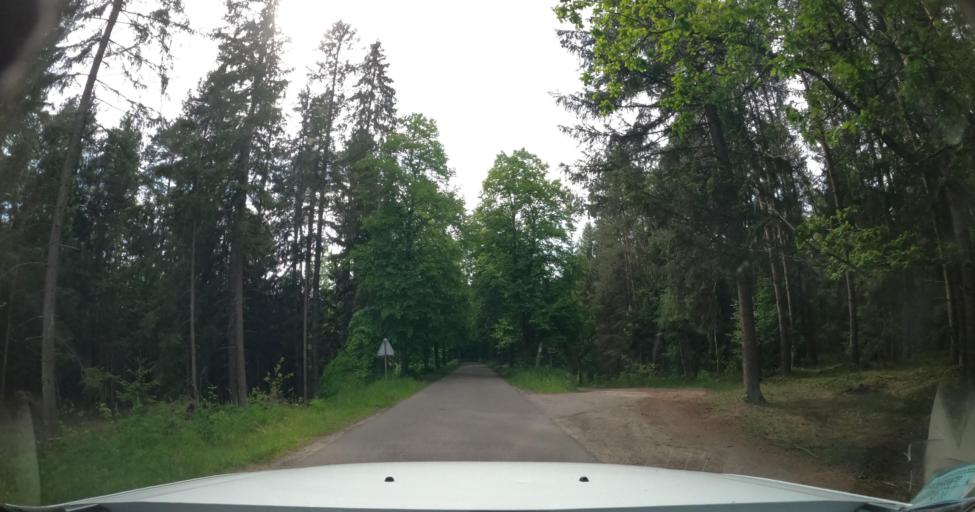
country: PL
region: Warmian-Masurian Voivodeship
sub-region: Powiat lidzbarski
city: Lubomino
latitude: 54.1047
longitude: 20.3553
